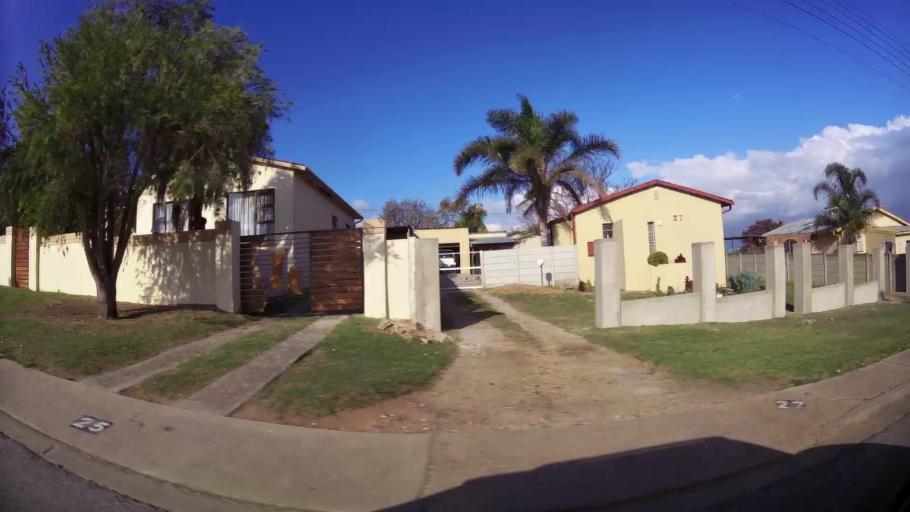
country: ZA
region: Eastern Cape
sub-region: Nelson Mandela Bay Metropolitan Municipality
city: Uitenhage
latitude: -33.7750
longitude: 25.4275
